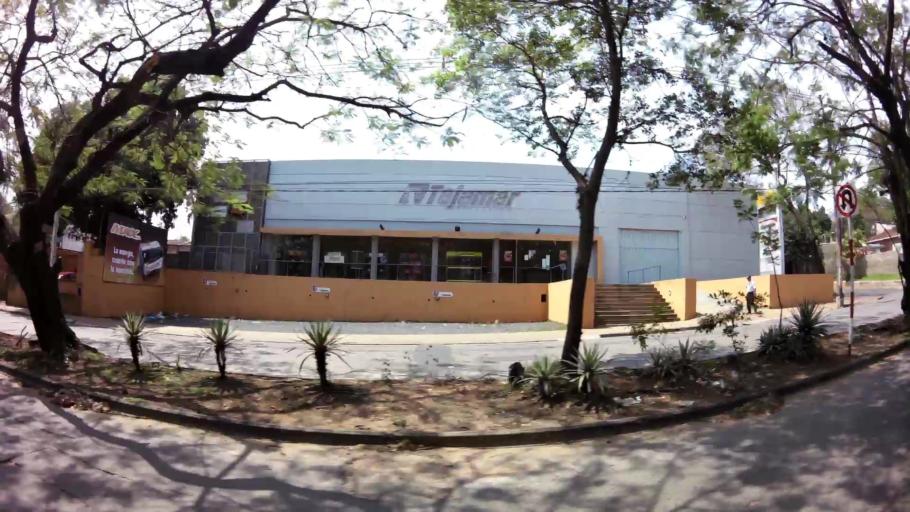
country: PY
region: Central
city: Lambare
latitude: -25.3104
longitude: -57.5969
